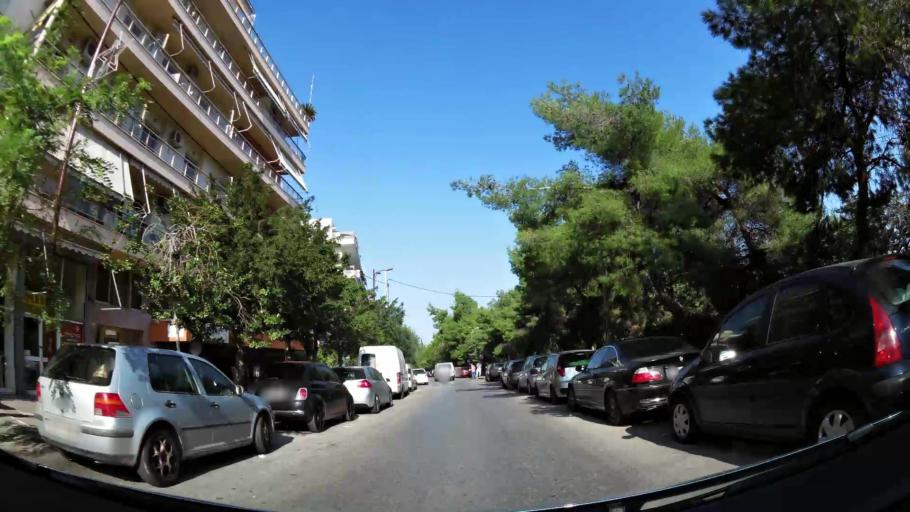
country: GR
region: Attica
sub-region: Nomos Attikis
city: Zografos
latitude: 37.9738
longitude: 23.7805
